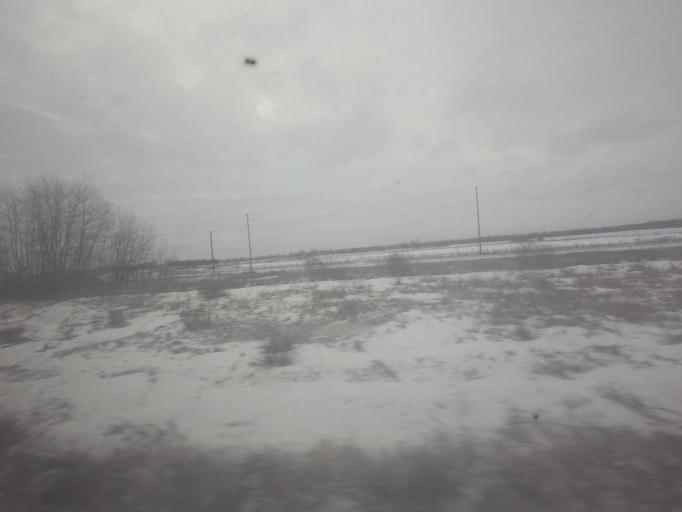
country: CA
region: Ontario
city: Bells Corners
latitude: 45.2595
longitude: -75.7753
